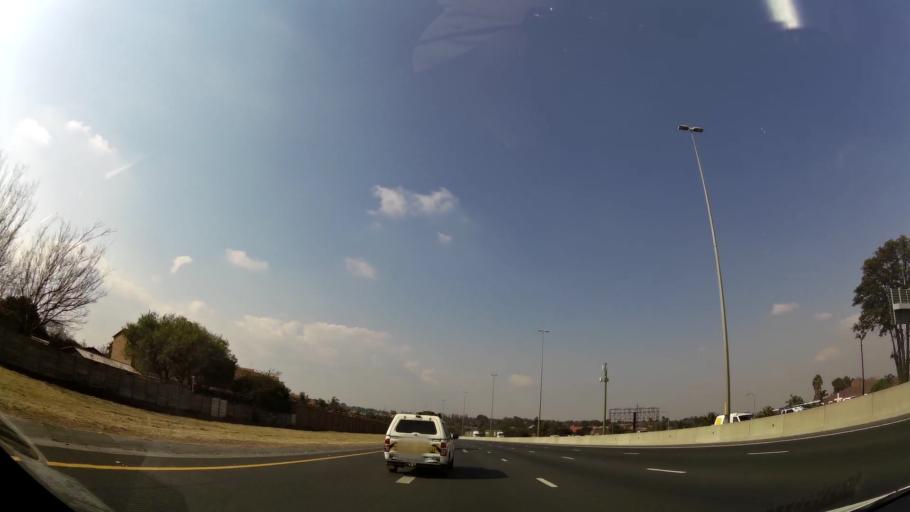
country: ZA
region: Gauteng
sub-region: Ekurhuleni Metropolitan Municipality
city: Germiston
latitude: -26.1777
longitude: 28.2019
